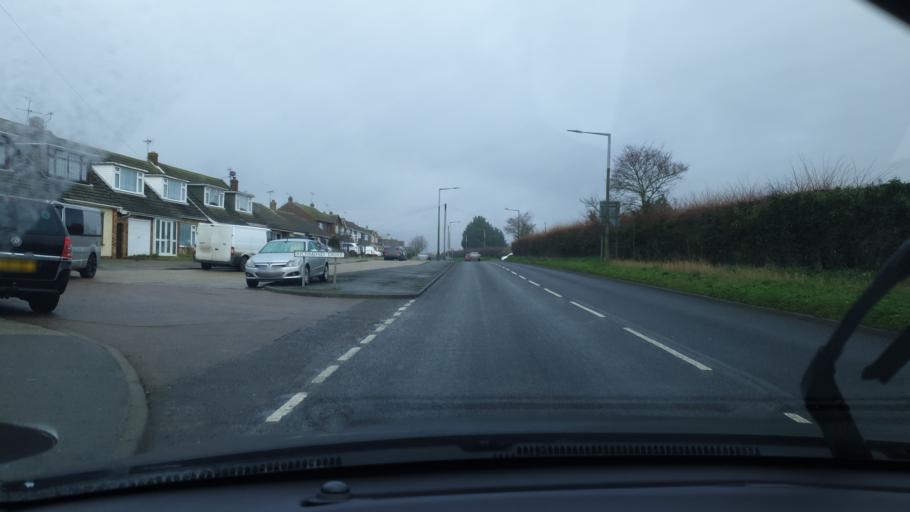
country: GB
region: England
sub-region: Essex
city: Clacton-on-Sea
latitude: 51.7833
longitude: 1.1202
